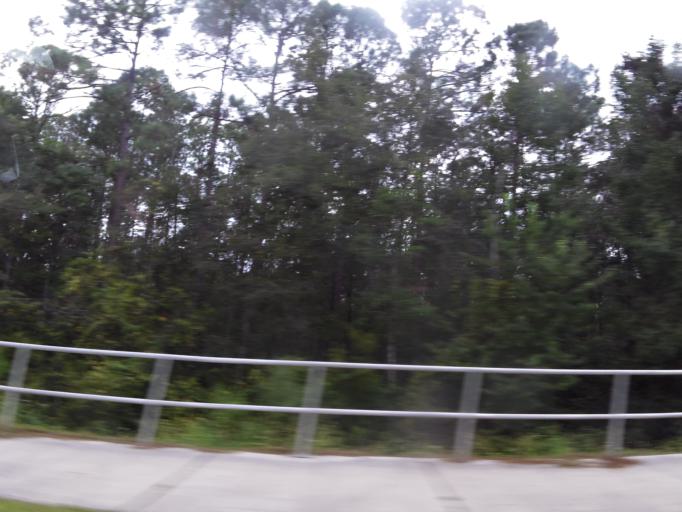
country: US
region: Florida
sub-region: Clay County
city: Asbury Lake
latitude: 30.0670
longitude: -81.8098
